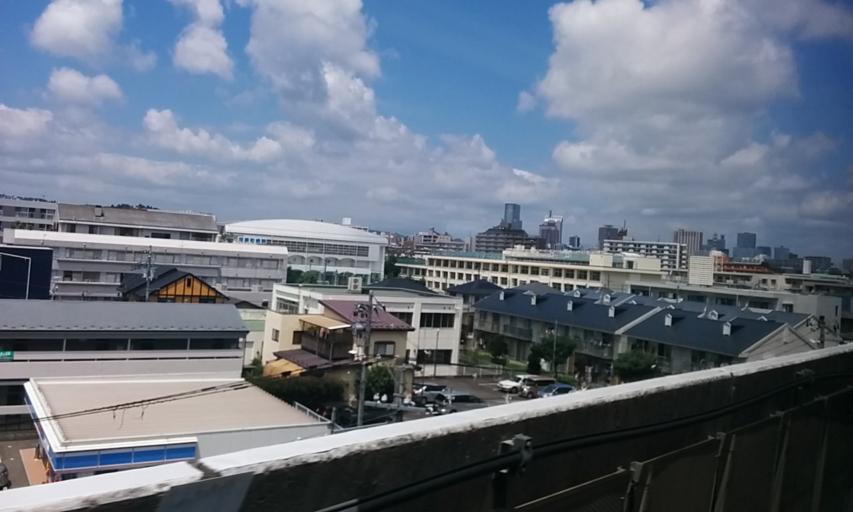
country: JP
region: Miyagi
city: Sendai
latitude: 38.2399
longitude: 140.8942
